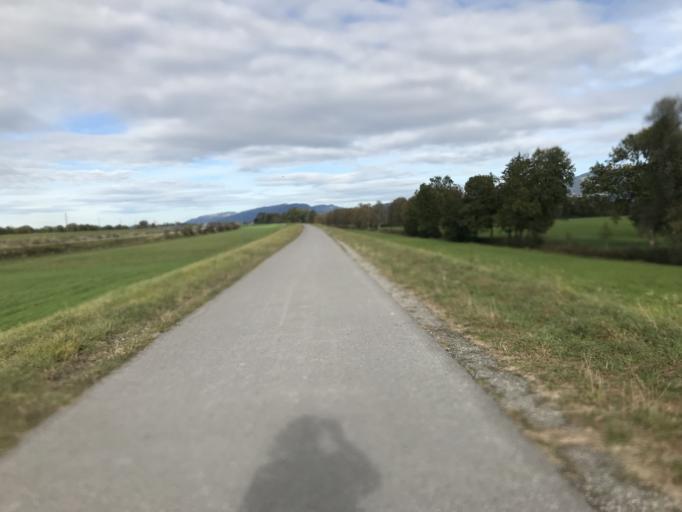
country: AT
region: Vorarlberg
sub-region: Politischer Bezirk Feldkirch
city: Mader
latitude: 47.3699
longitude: 9.6313
